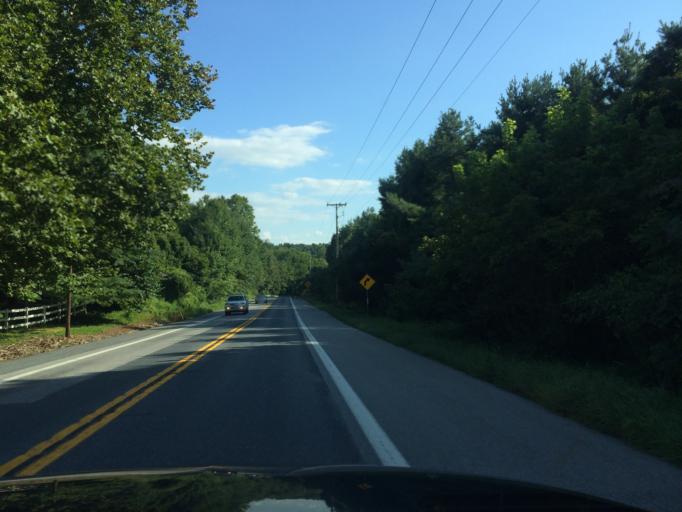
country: US
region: Maryland
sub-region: Montgomery County
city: Olney
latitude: 39.2597
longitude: -77.0505
